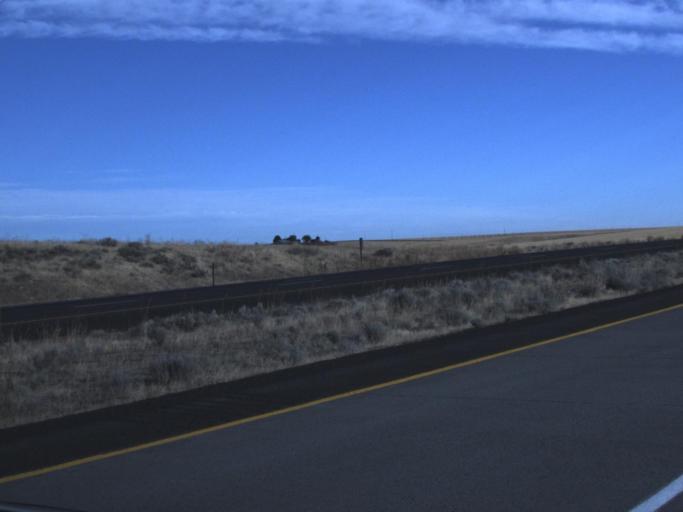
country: US
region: Washington
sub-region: Adams County
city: Ritzville
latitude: 46.9280
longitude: -118.5935
